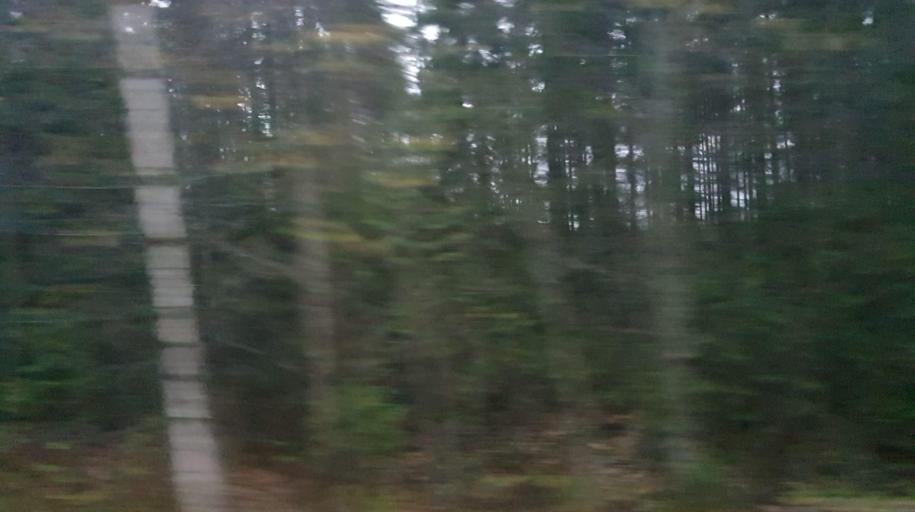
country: NO
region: Buskerud
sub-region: Krodsherad
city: Noresund
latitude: 60.1871
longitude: 9.5971
